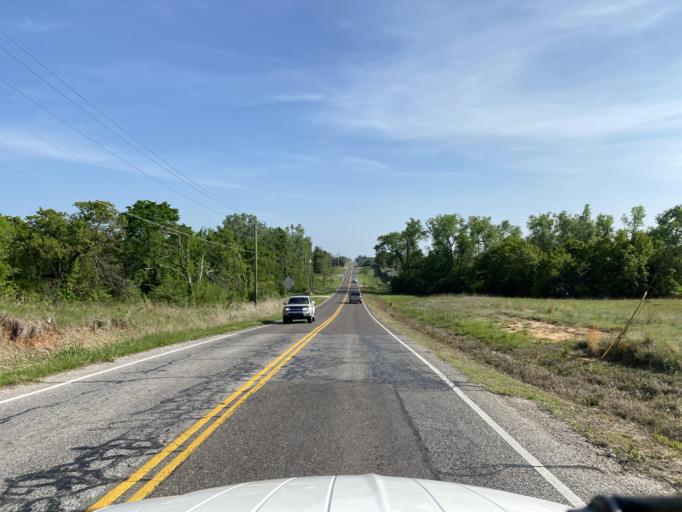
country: US
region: Oklahoma
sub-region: Oklahoma County
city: Nicoma Park
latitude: 35.4784
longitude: -97.3356
